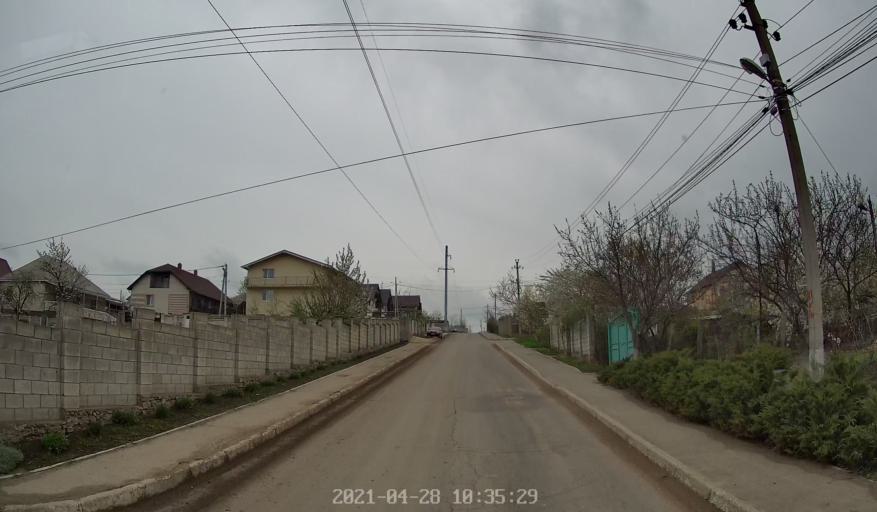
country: MD
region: Chisinau
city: Singera
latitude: 46.9881
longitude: 28.9391
